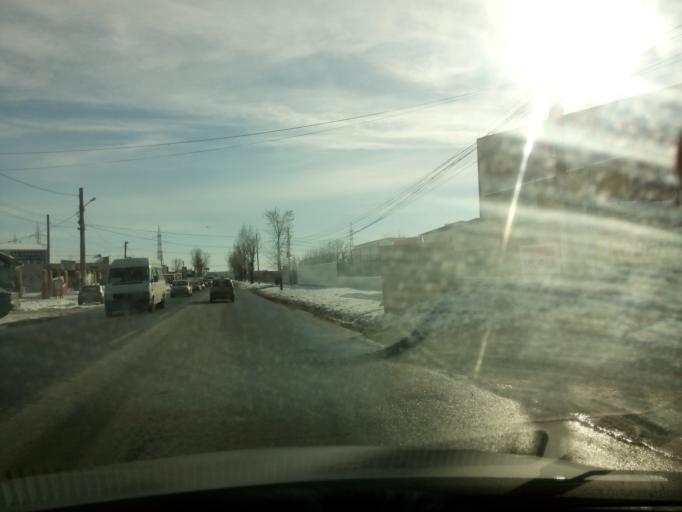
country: RO
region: Ilfov
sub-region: Comuna Popesti-Leordeni
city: Popesti-Leordeni
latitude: 44.3719
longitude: 26.1805
